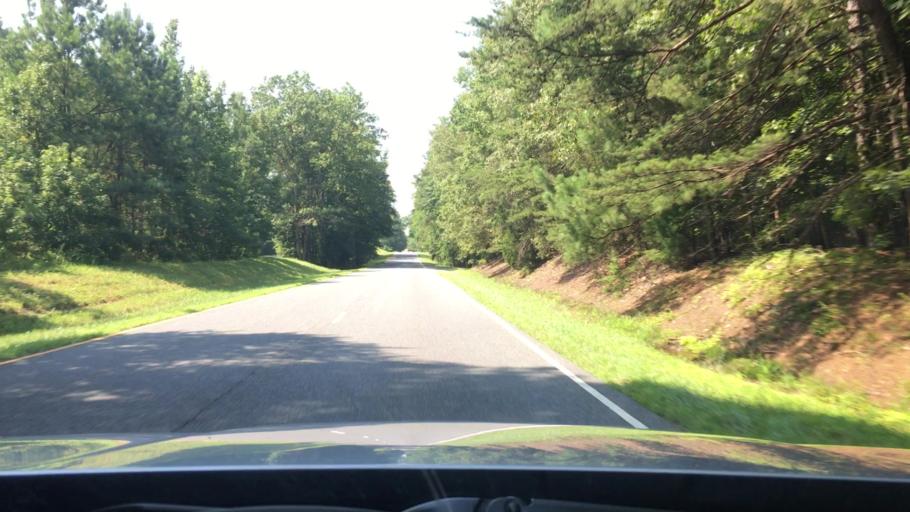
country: US
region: Virginia
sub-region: Caroline County
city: Bowling Green
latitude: 37.9571
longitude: -77.4402
